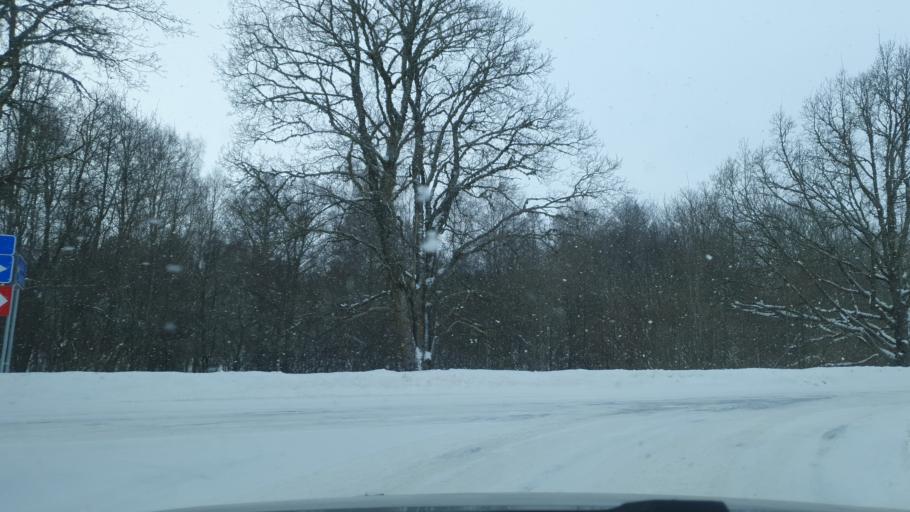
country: EE
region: Harju
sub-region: Kuusalu vald
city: Kuusalu
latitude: 59.4810
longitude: 25.3412
